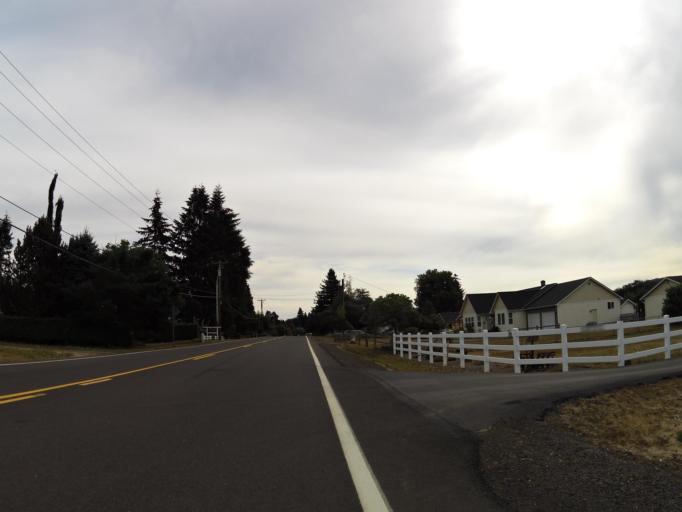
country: US
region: Washington
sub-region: Cowlitz County
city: West Side Highway
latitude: 46.2242
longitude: -122.8948
